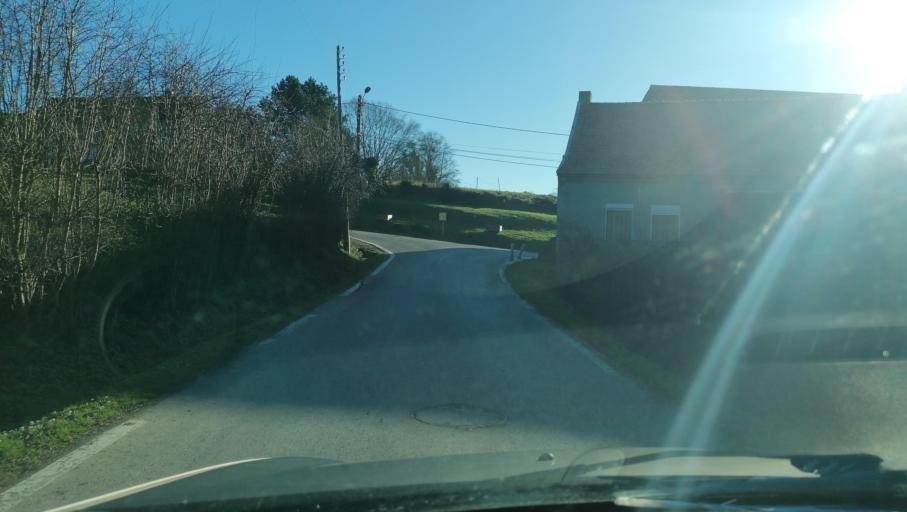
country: FR
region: Nord-Pas-de-Calais
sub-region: Departement du Nord
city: Ferriere-la-Grande
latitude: 50.2187
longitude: 4.0270
